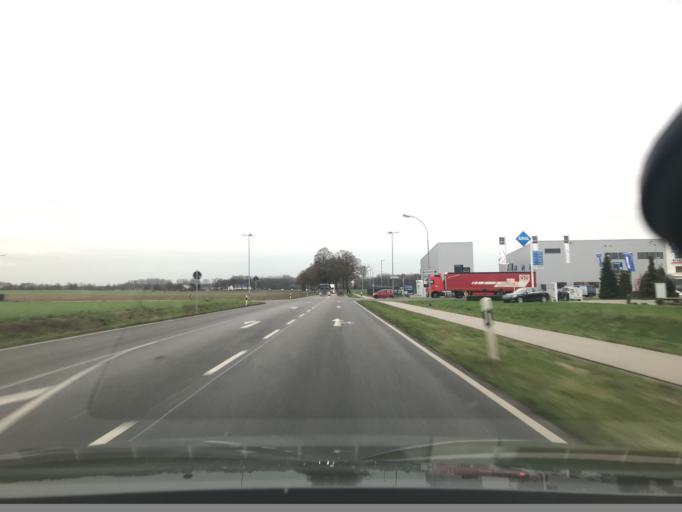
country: DE
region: North Rhine-Westphalia
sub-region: Regierungsbezirk Dusseldorf
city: Uedem
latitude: 51.6591
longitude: 6.2761
